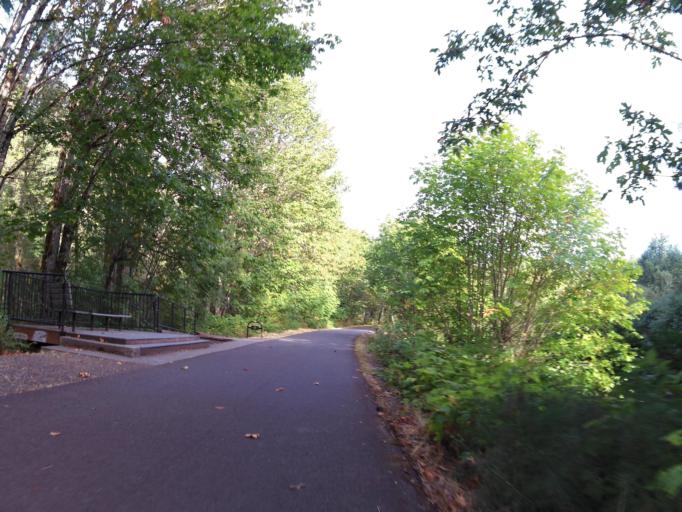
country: US
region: Washington
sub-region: Thurston County
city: Tenino
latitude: 46.9282
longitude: -122.8142
